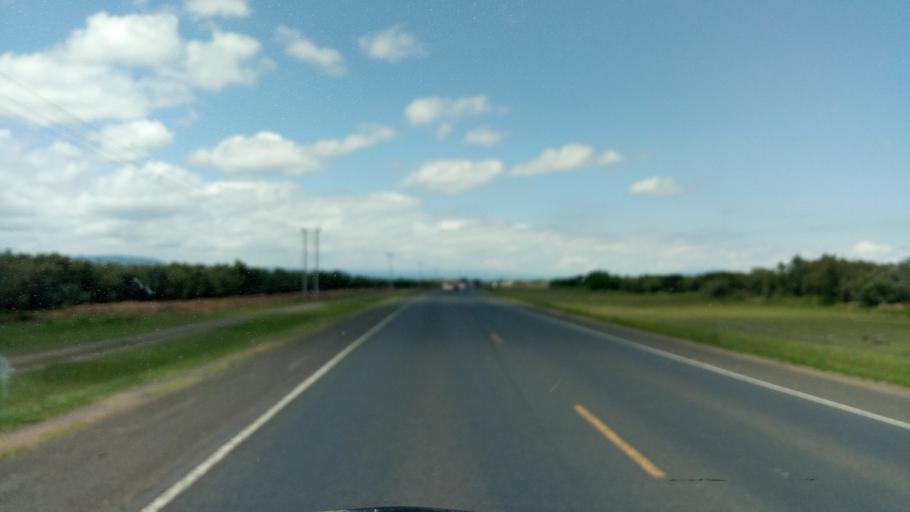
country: KE
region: Nakuru
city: Naivasha
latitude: -0.5500
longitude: 36.3472
